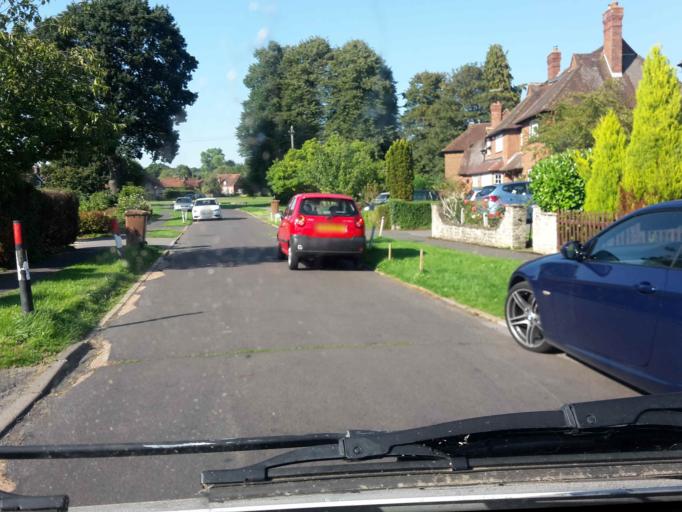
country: GB
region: England
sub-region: Surrey
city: Chilworth
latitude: 51.1828
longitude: -0.5263
